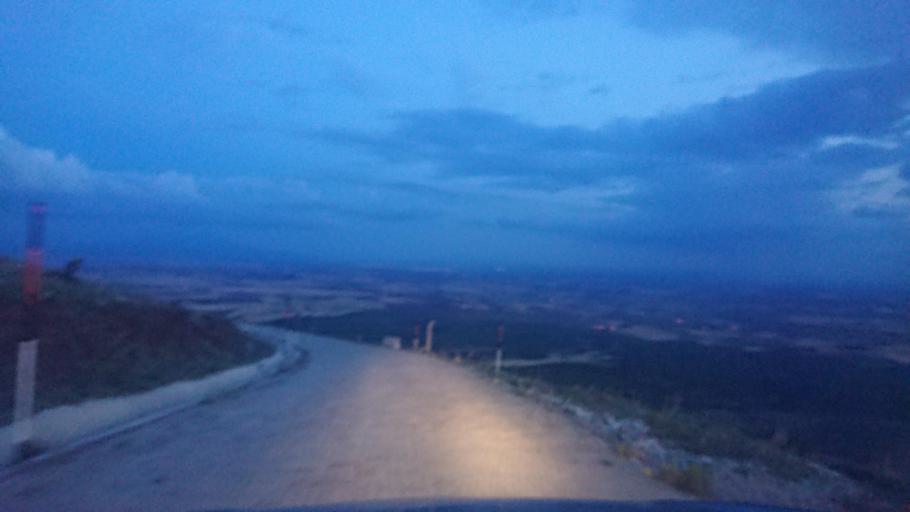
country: TR
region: Aksaray
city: Ortakoy
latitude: 38.6405
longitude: 34.0268
